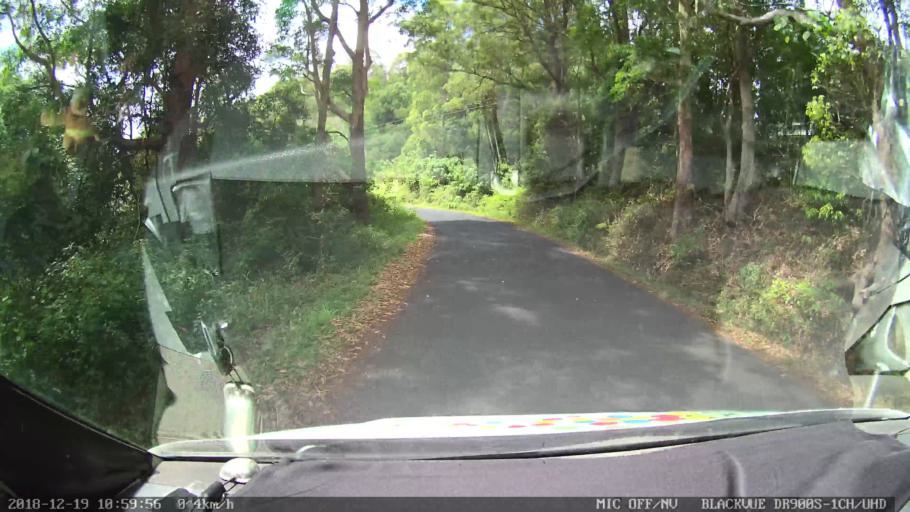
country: AU
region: New South Wales
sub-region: Lismore Municipality
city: Nimbin
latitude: -28.5996
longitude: 153.2616
